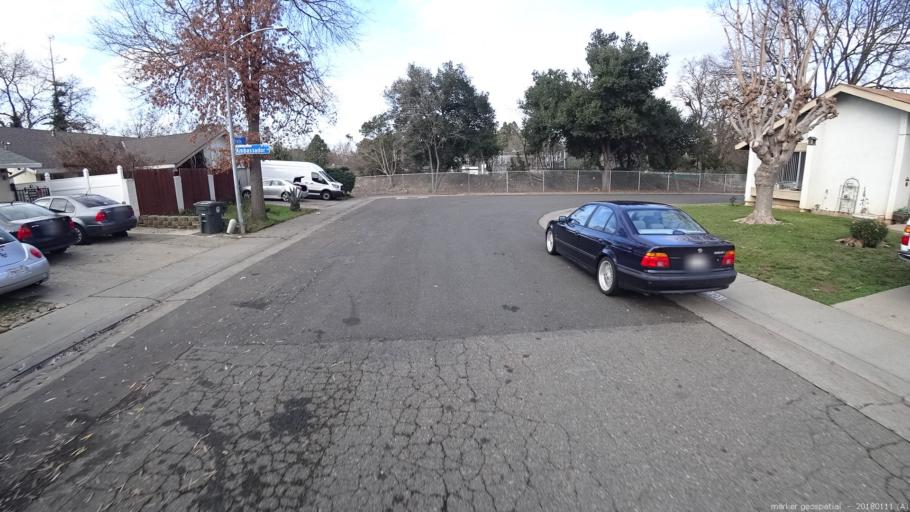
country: US
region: California
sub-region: Sacramento County
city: Rancho Cordova
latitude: 38.6046
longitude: -121.3062
